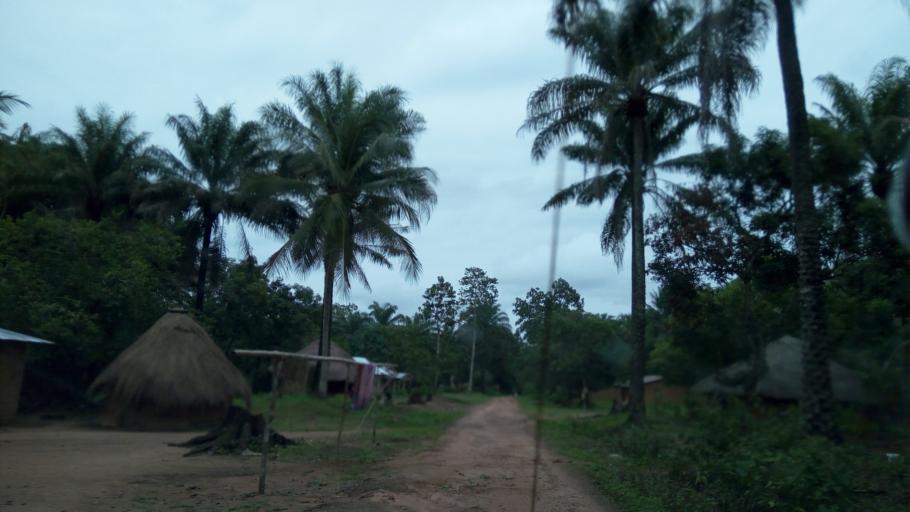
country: SL
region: Northern Province
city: Kassiri
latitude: 9.0375
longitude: -13.0999
